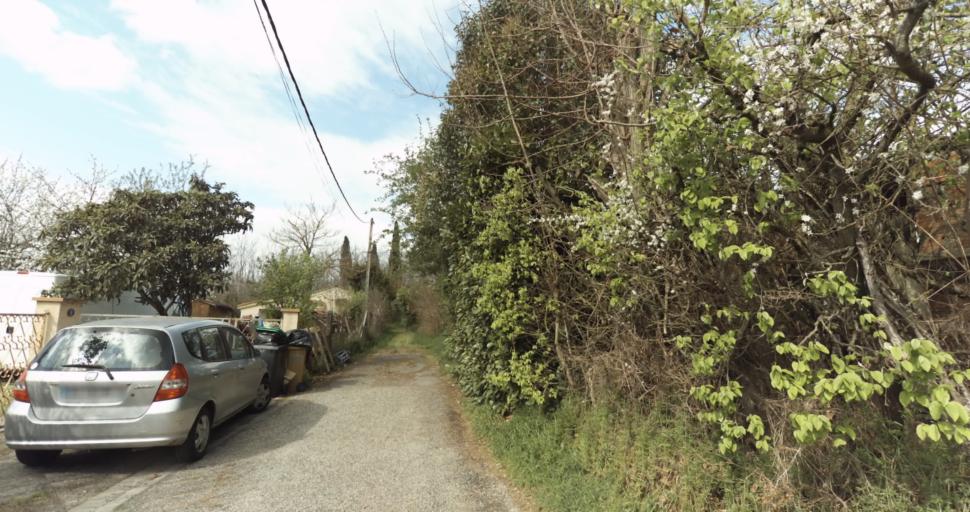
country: FR
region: Midi-Pyrenees
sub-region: Departement de la Haute-Garonne
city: Auterive
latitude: 43.3590
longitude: 1.4760
